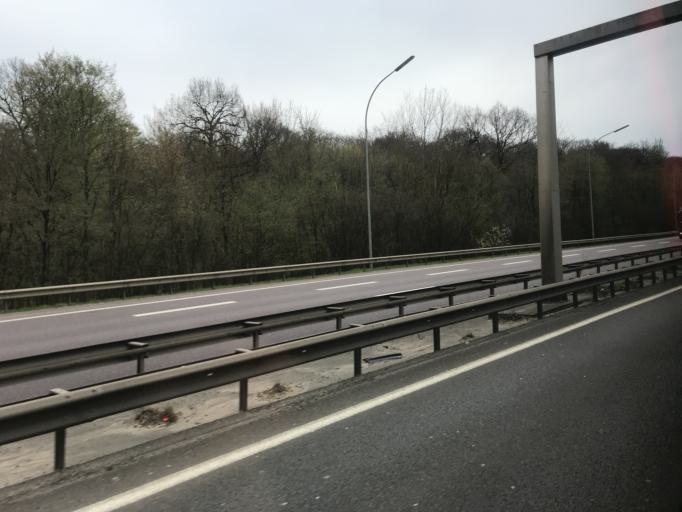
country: LU
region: Luxembourg
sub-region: Canton d'Esch-sur-Alzette
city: Leudelange
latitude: 49.5722
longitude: 6.0882
